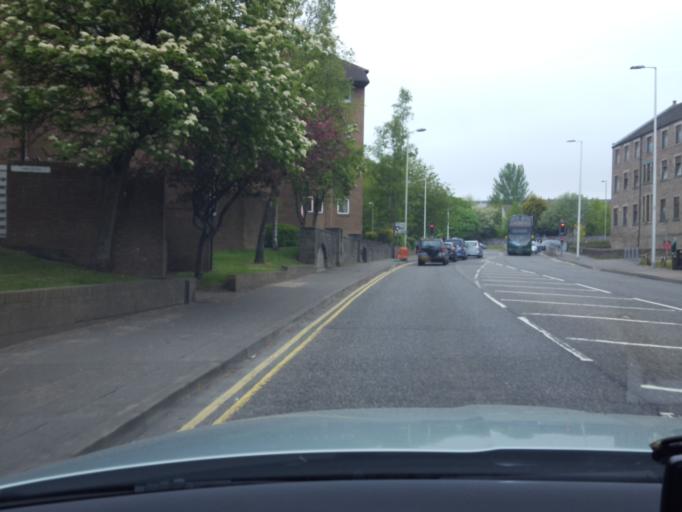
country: GB
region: Scotland
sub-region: Dundee City
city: Dundee
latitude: 56.4689
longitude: -2.9635
